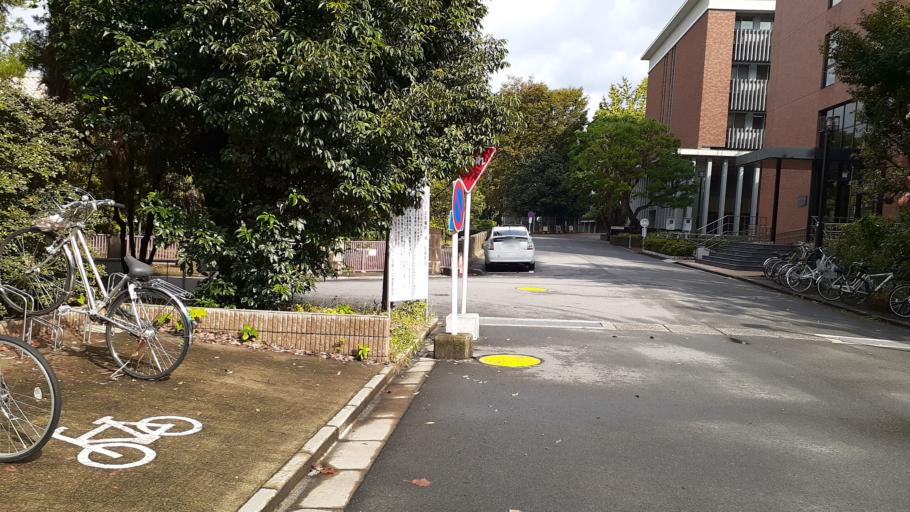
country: JP
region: Kyoto
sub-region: Kyoto-shi
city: Kamigyo-ku
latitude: 35.0309
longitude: 135.7857
